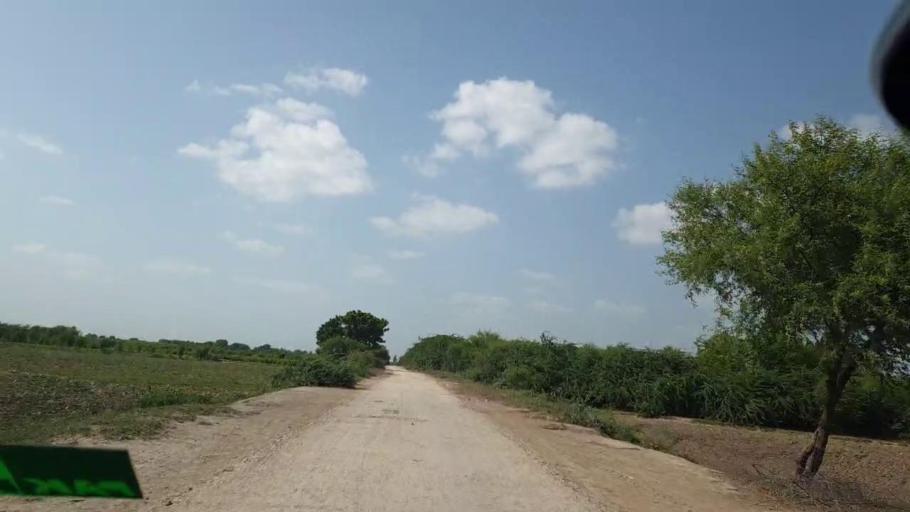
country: PK
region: Sindh
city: Naukot
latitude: 24.6479
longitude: 69.2214
